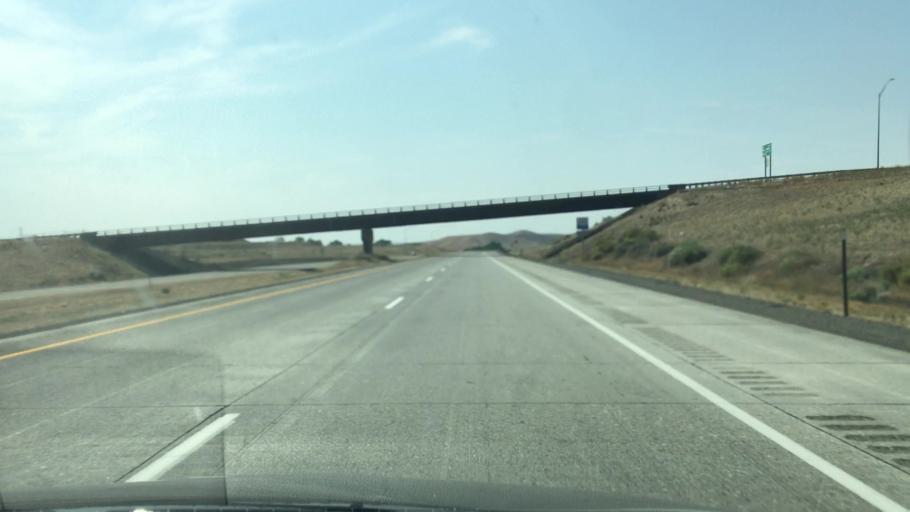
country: US
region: Idaho
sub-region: Elmore County
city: Glenns Ferry
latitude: 42.9602
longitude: -115.2887
